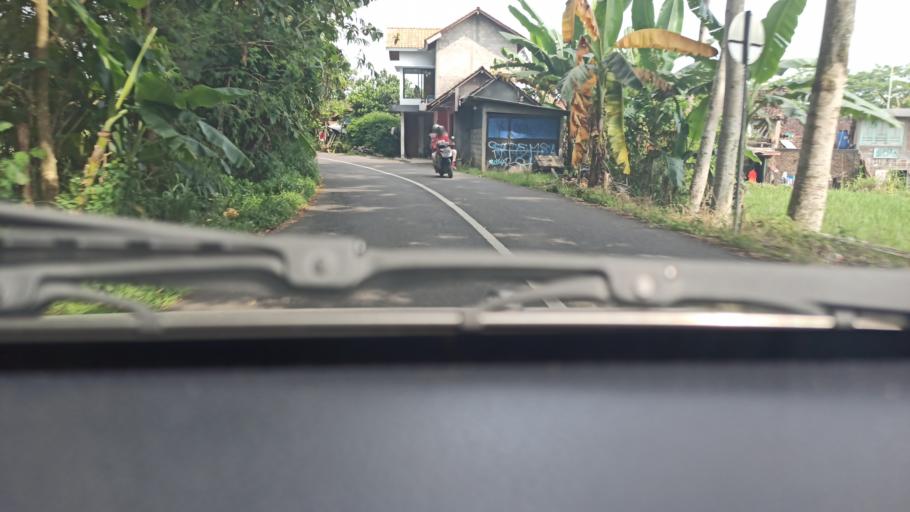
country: ID
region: Daerah Istimewa Yogyakarta
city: Sleman
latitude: -7.7040
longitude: 110.2984
